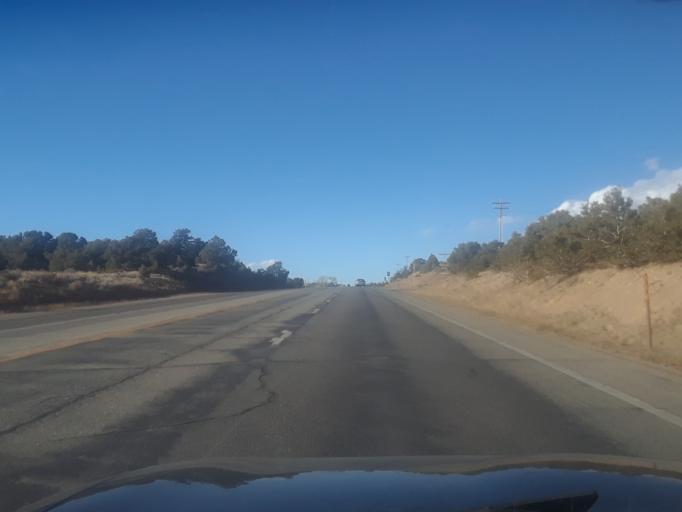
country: US
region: Colorado
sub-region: Chaffee County
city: Salida
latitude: 38.6585
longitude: -106.0870
